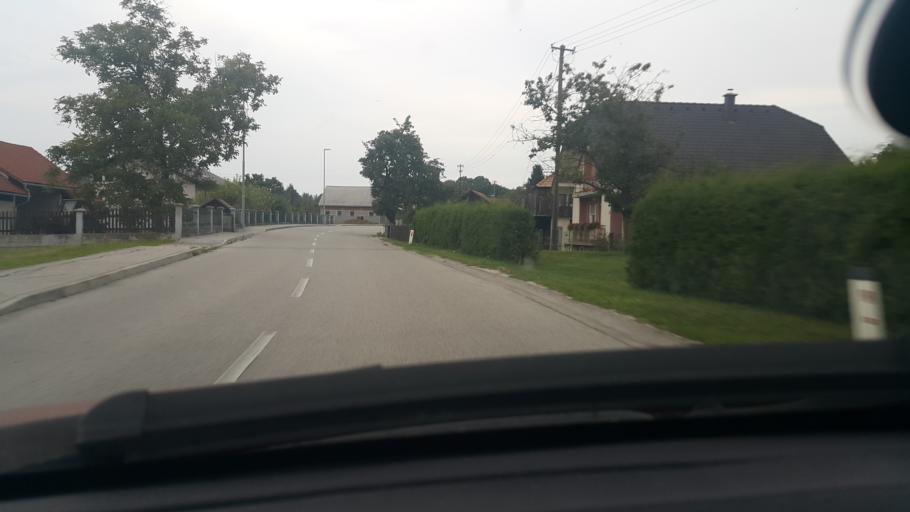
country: SI
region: Brezice
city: Brezice
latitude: 45.9271
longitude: 15.6720
